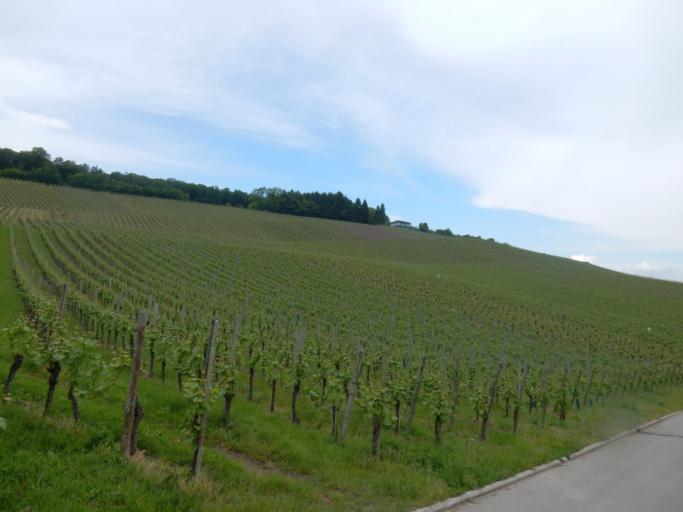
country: LU
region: Grevenmacher
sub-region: Canton de Remich
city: Bous
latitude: 49.5241
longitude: 6.3333
